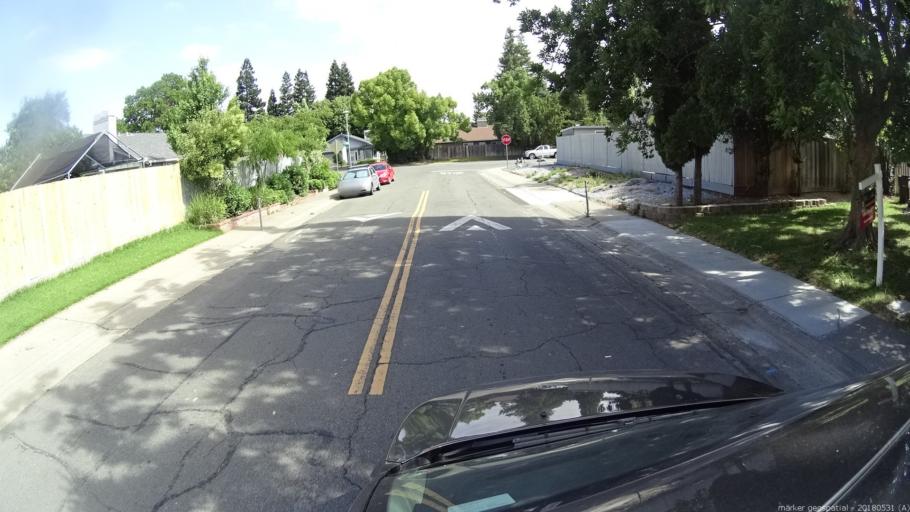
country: US
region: California
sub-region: Sacramento County
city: Sacramento
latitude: 38.6208
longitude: -121.5034
